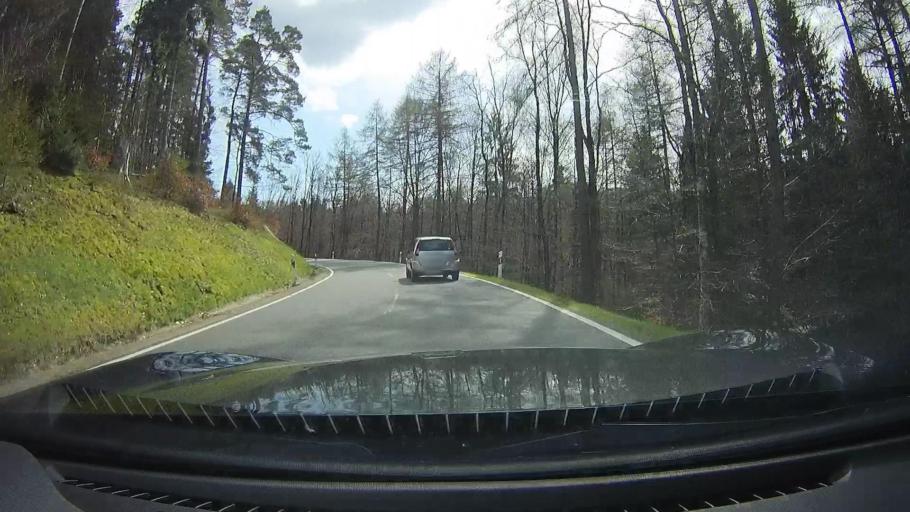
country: DE
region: Hesse
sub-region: Regierungsbezirk Darmstadt
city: Hesseneck
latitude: 49.5549
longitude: 9.1215
